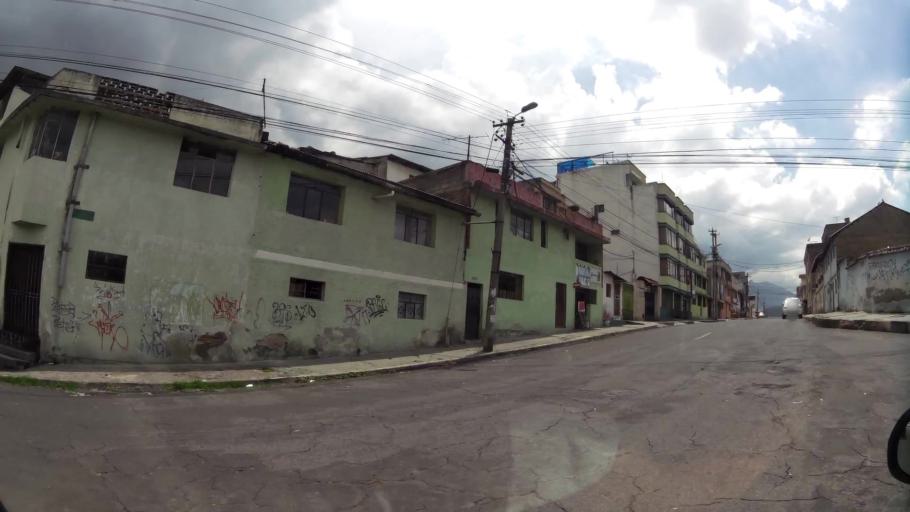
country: EC
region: Pichincha
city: Quito
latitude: -0.2579
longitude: -78.5191
